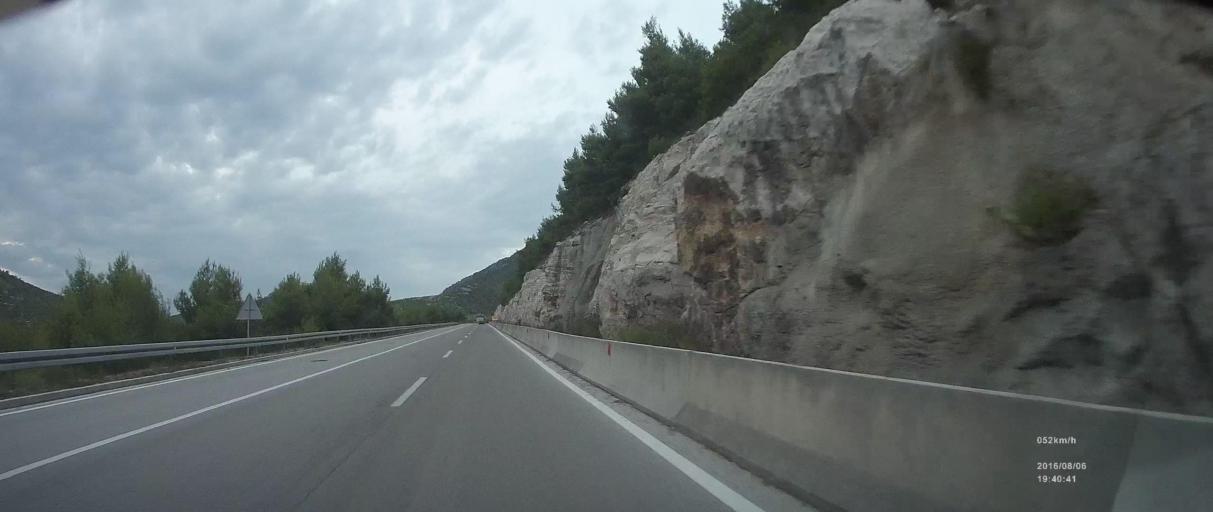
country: HR
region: Dubrovacko-Neretvanska
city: Ston
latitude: 42.8153
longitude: 17.6792
